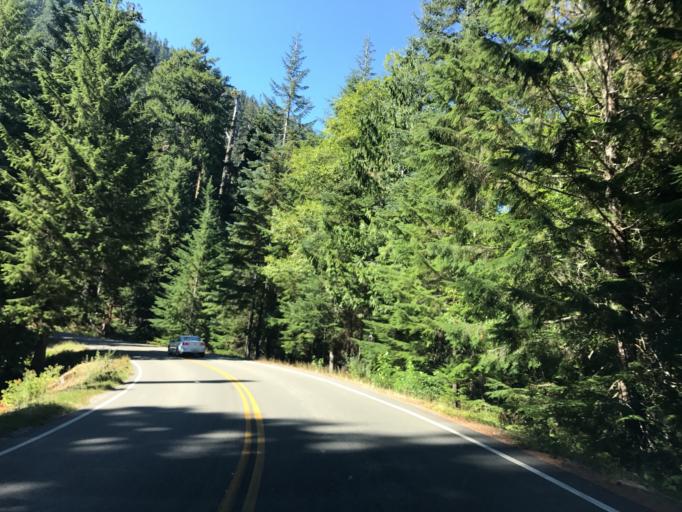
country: US
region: Washington
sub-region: Pierce County
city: Buckley
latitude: 46.7466
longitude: -121.5723
